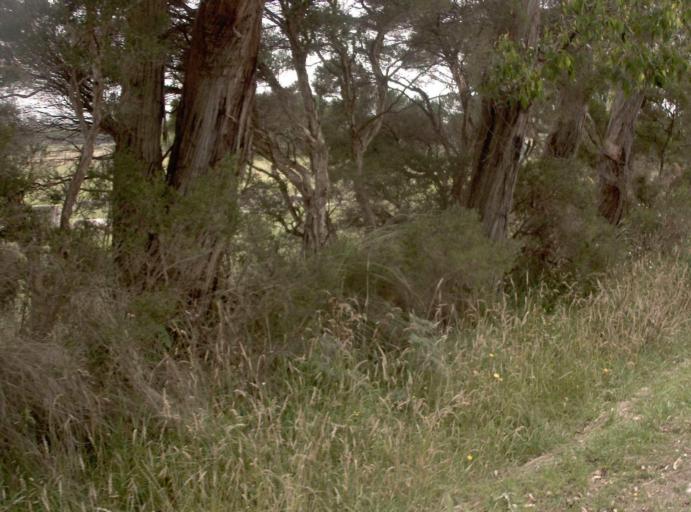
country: AU
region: Victoria
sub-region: Cardinia
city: Koo-Wee-Rup
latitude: -38.3422
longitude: 145.6594
